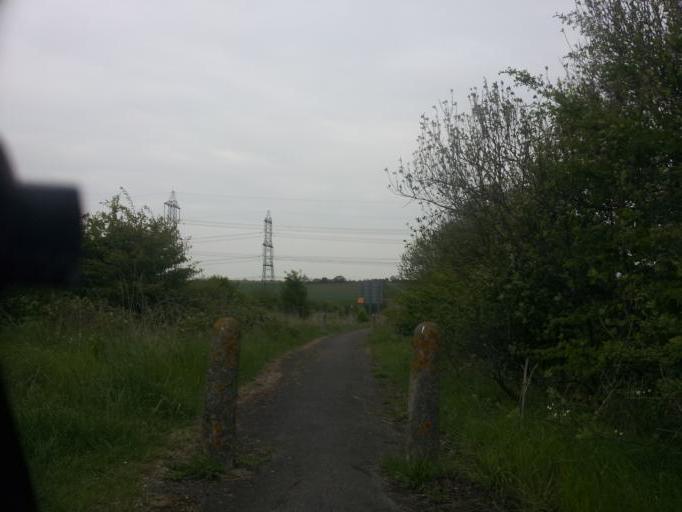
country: GB
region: England
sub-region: Medway
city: High Halstow
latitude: 51.4364
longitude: 0.5684
